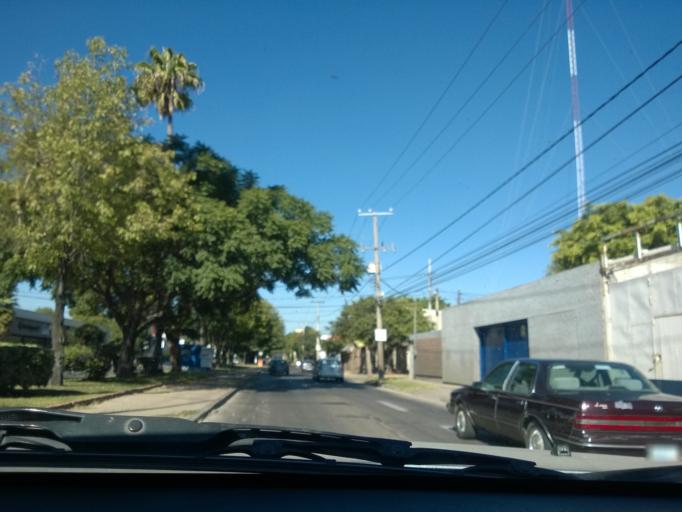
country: MX
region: Guanajuato
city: Leon
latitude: 21.1088
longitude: -101.6648
